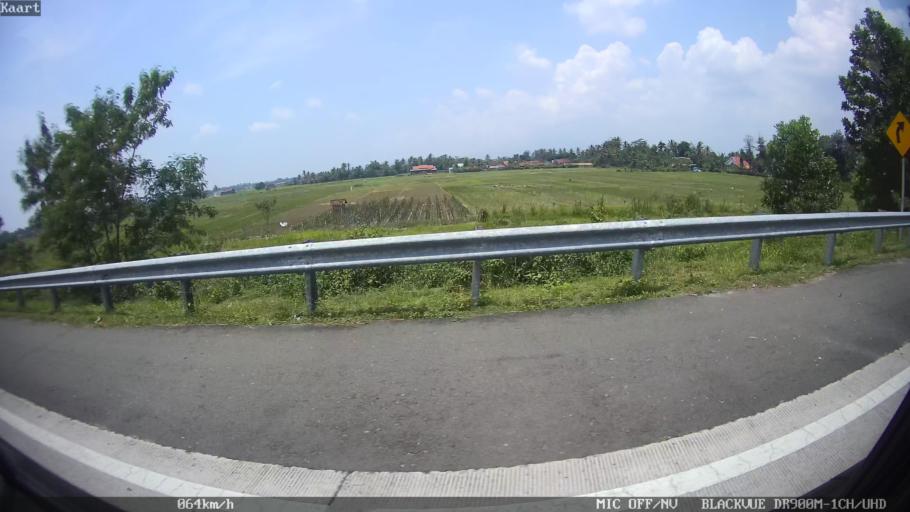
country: ID
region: Lampung
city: Natar
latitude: -5.2922
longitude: 105.2316
